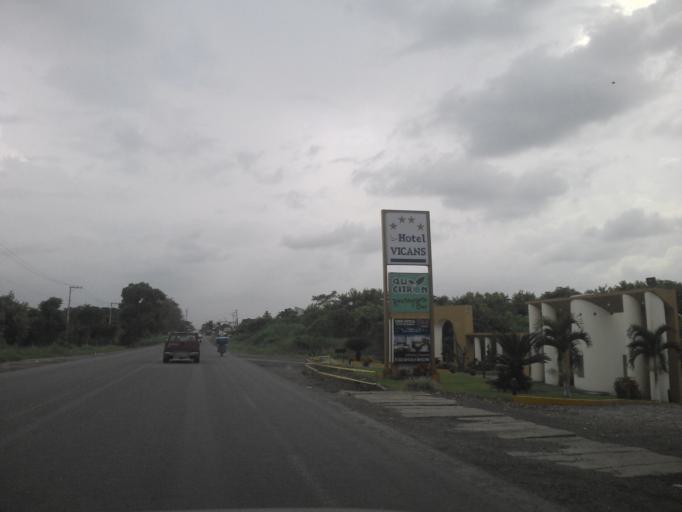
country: MX
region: Veracruz
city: Martinez de la Torre
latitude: 20.0787
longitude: -97.0493
